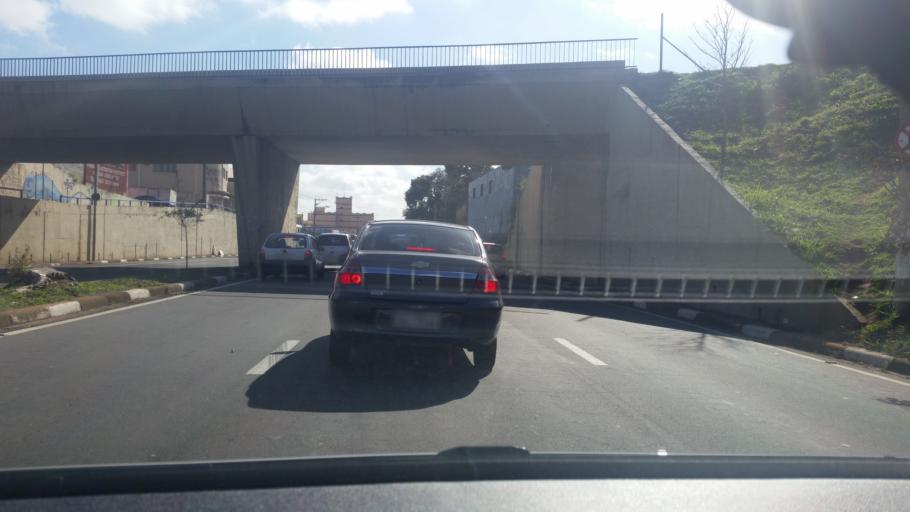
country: BR
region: Sao Paulo
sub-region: Campinas
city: Campinas
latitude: -22.9027
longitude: -47.0728
